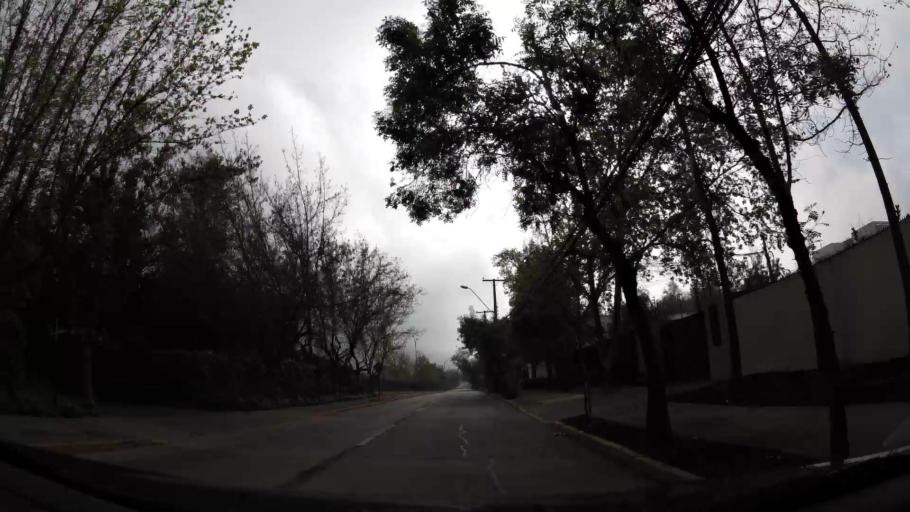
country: CL
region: Santiago Metropolitan
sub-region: Provincia de Santiago
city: Villa Presidente Frei, Nunoa, Santiago, Chile
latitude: -33.3792
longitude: -70.5327
